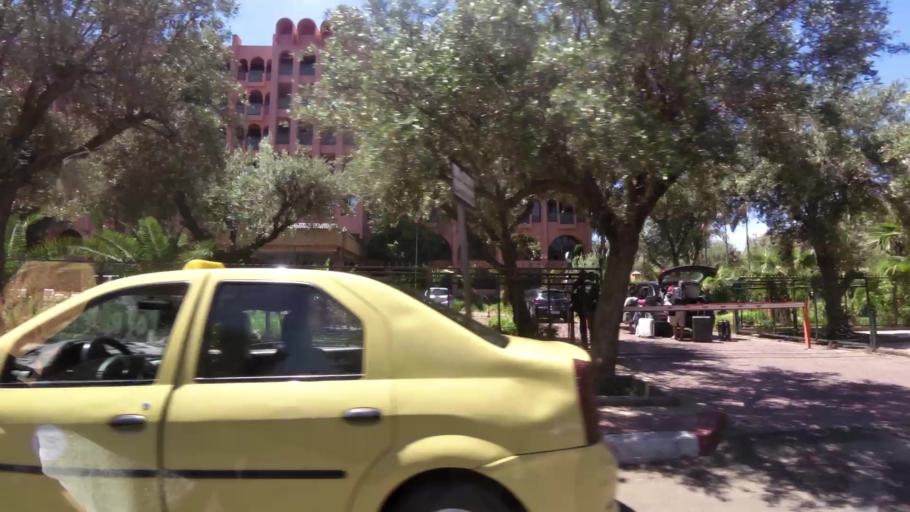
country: MA
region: Marrakech-Tensift-Al Haouz
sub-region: Marrakech
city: Marrakesh
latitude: 31.6212
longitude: -8.0068
